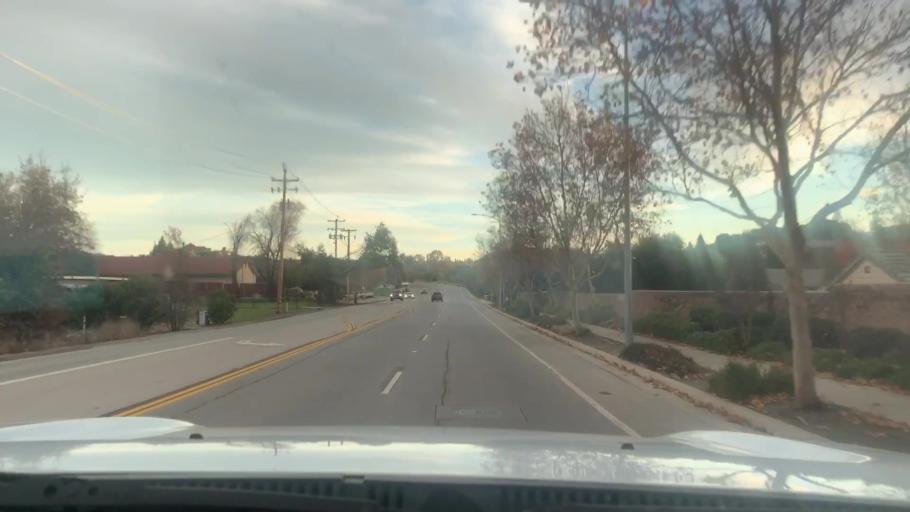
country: US
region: California
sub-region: San Luis Obispo County
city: Paso Robles
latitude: 35.6383
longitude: -120.6582
